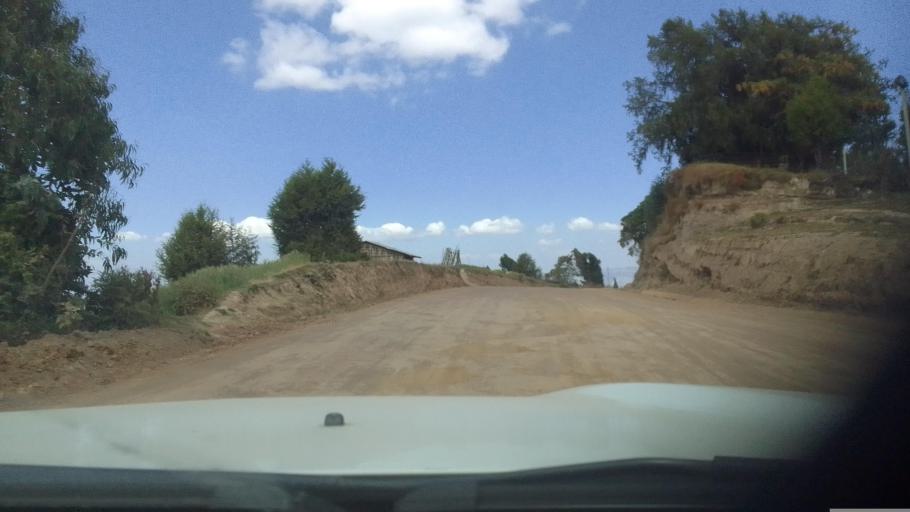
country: ET
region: Oromiya
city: Hagere Hiywet
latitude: 8.8418
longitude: 37.8853
